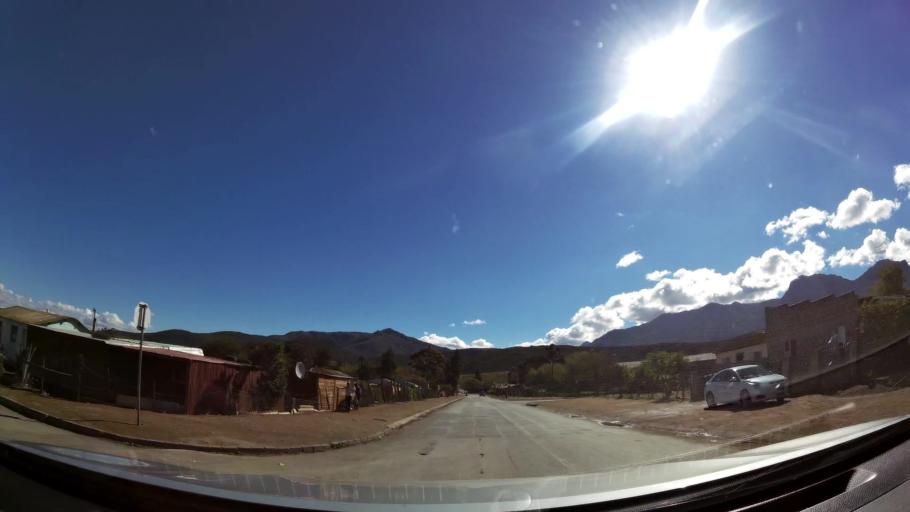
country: ZA
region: Western Cape
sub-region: Cape Winelands District Municipality
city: Ashton
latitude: -33.7893
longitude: 19.8903
